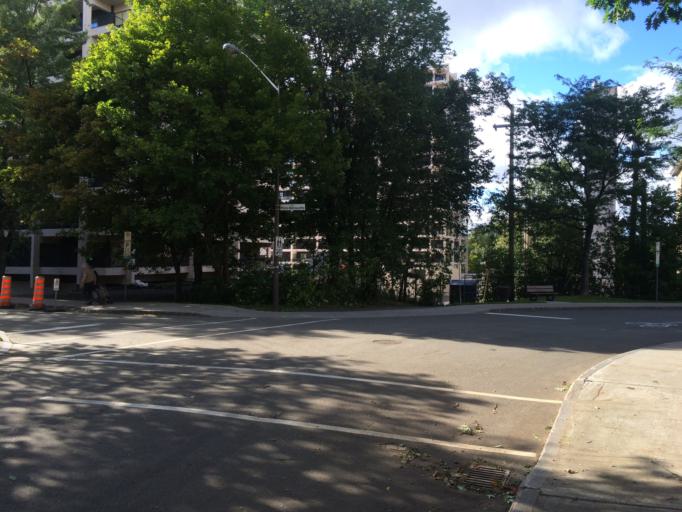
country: CA
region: Quebec
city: Quebec
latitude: 46.8025
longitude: -71.2324
